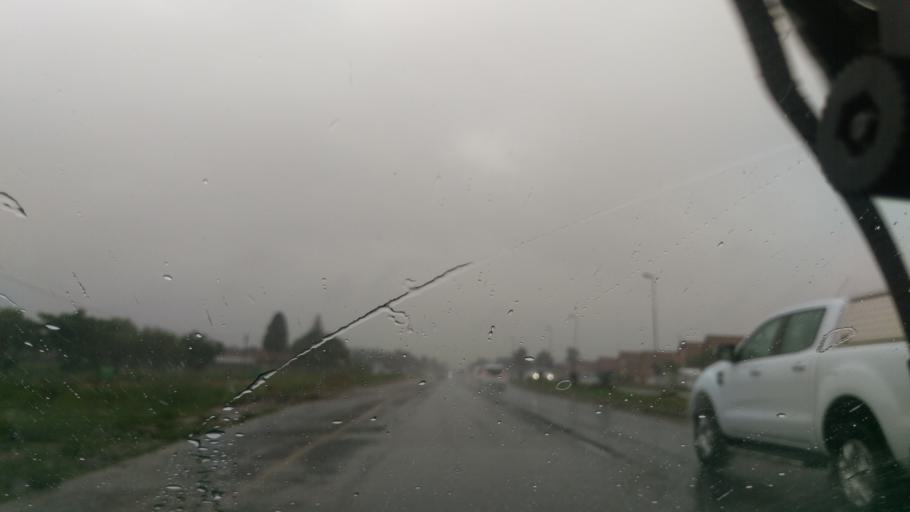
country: ZA
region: Gauteng
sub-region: West Rand District Municipality
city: Muldersdriseloop
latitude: -26.0457
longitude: 27.9540
